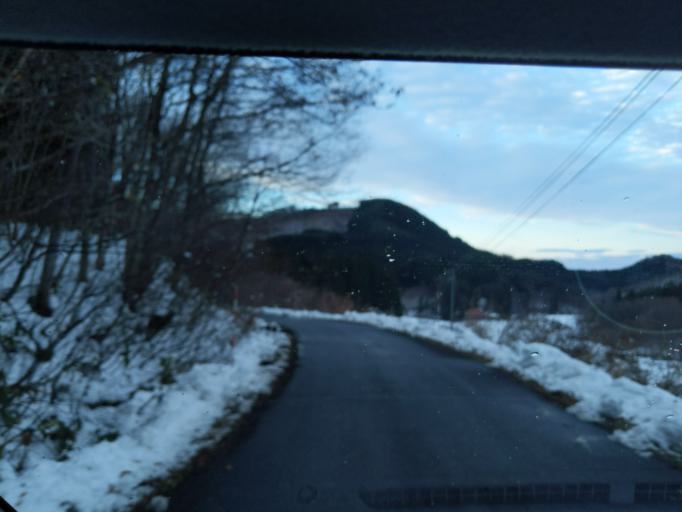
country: JP
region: Iwate
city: Mizusawa
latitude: 39.0435
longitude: 141.0203
